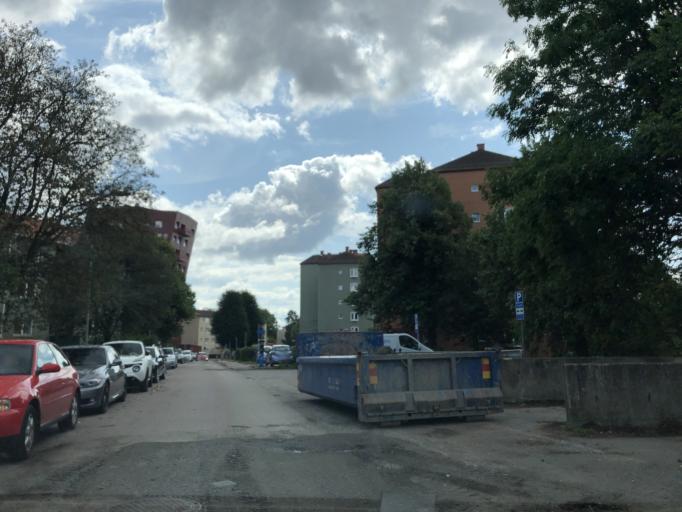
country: SE
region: Vaestra Goetaland
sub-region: Goteborg
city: Majorna
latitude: 57.7141
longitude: 11.9116
